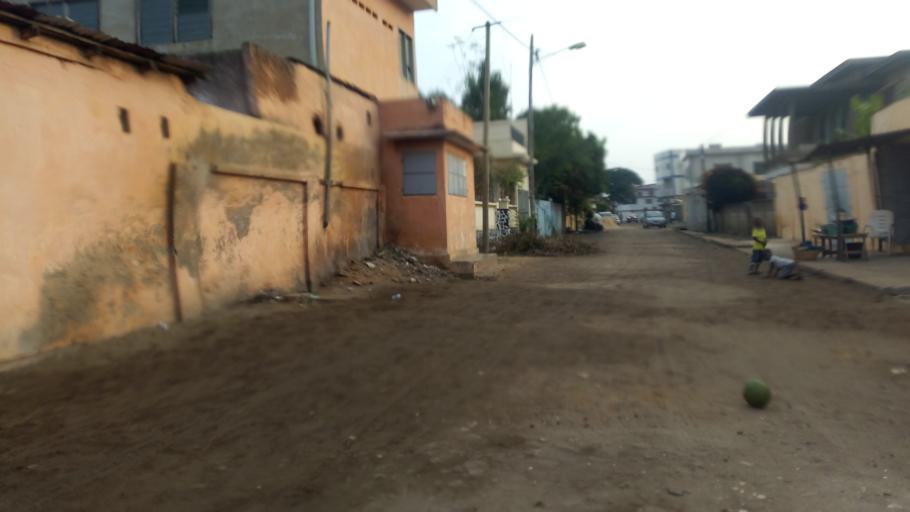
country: TG
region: Maritime
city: Lome
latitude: 6.1365
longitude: 1.2138
